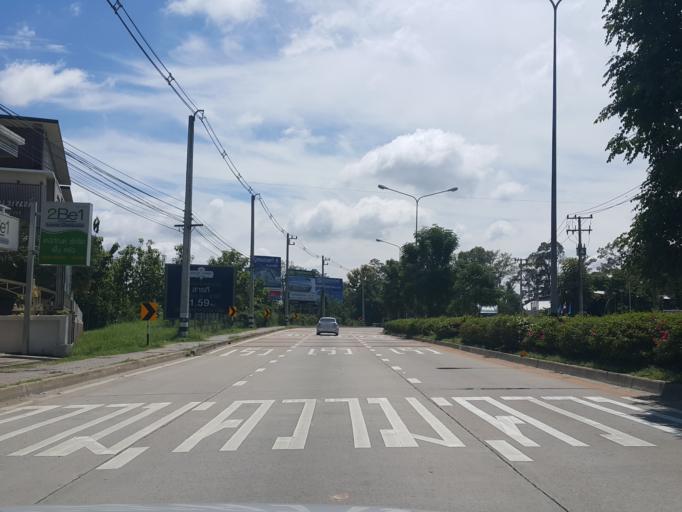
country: TH
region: Chiang Mai
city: Saraphi
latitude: 18.7459
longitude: 99.0167
